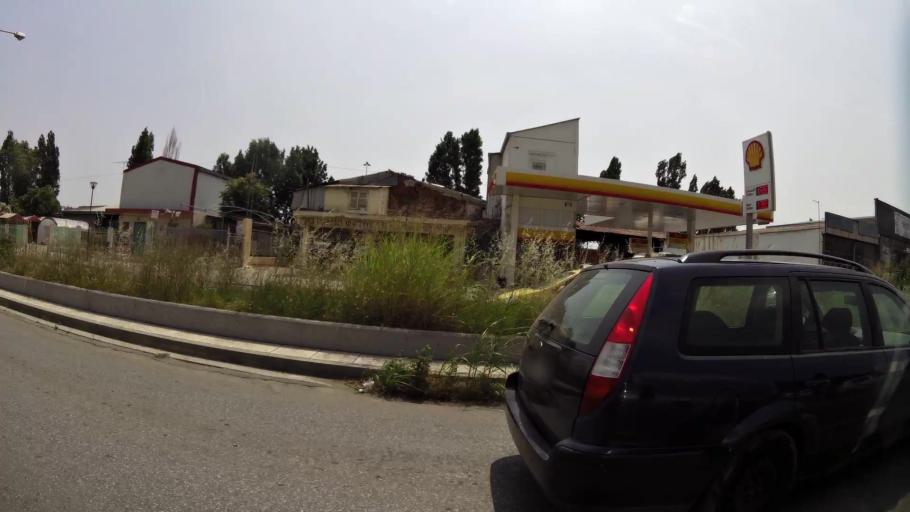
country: GR
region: Central Macedonia
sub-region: Nomos Thessalonikis
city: Menemeni
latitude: 40.6647
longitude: 22.8951
